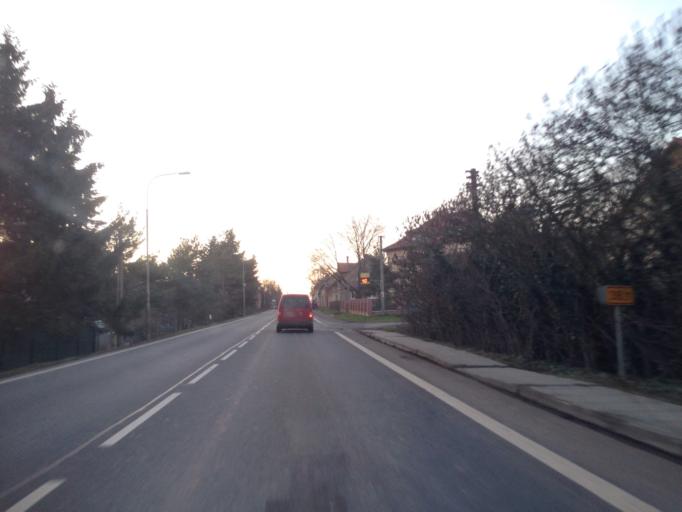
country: CZ
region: Central Bohemia
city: Revnicov
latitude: 50.1811
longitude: 13.8124
